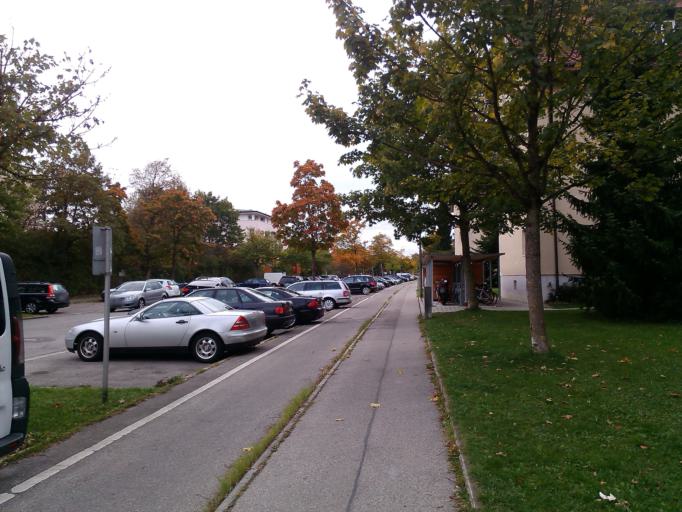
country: DE
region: Bavaria
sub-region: Upper Bavaria
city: Grafelfing
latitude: 48.1207
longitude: 11.4329
